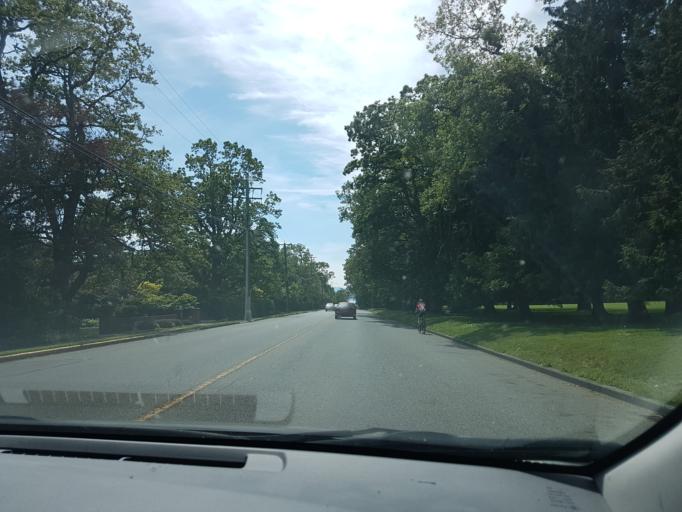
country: CA
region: British Columbia
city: Oak Bay
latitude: 48.4490
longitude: -123.3091
